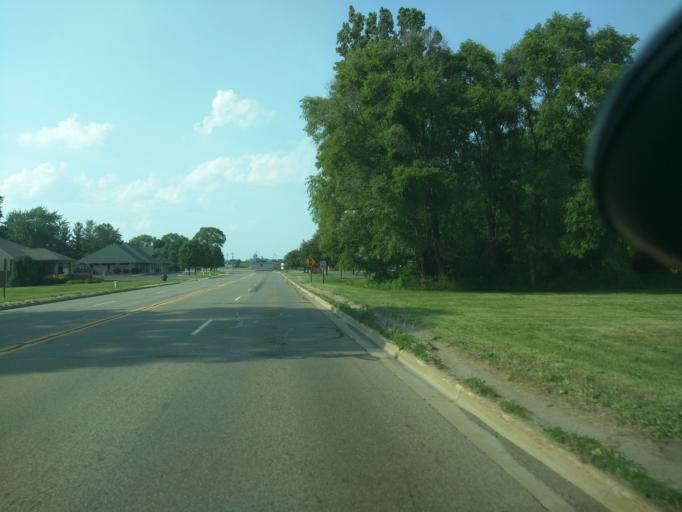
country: US
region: Michigan
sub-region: Jackson County
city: Jackson
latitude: 42.2588
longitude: -84.4477
